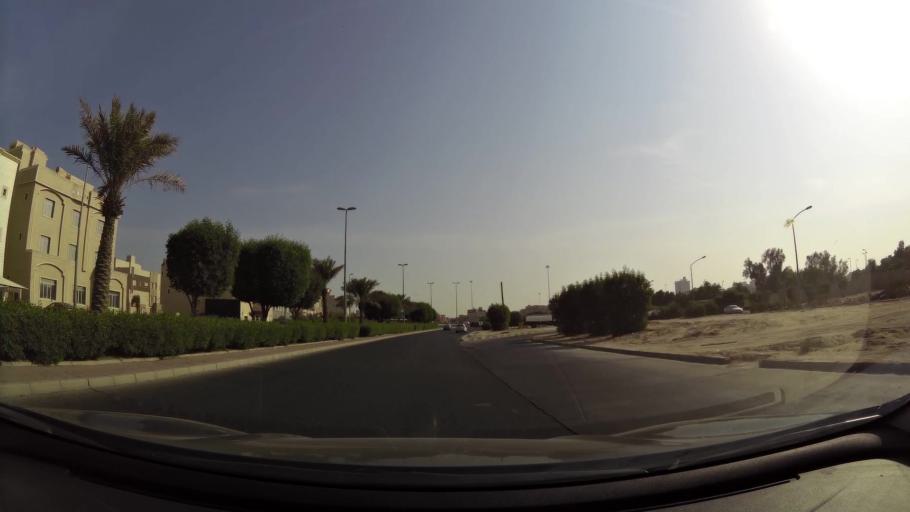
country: KW
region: Mubarak al Kabir
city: Mubarak al Kabir
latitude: 29.1841
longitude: 48.1015
